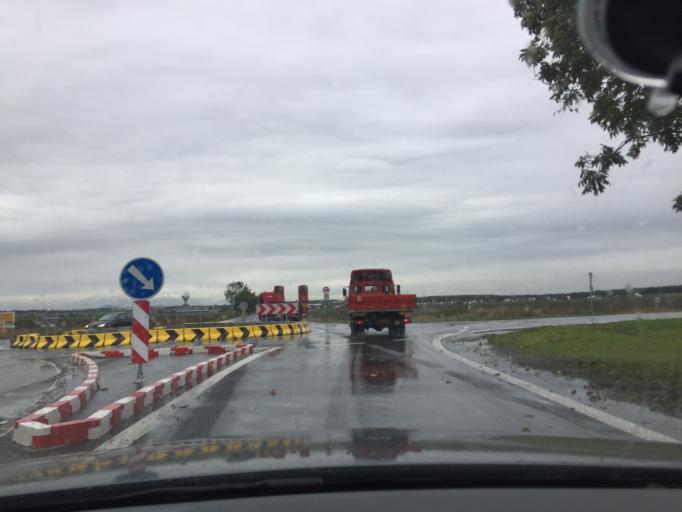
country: CZ
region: Central Bohemia
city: Zdiby
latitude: 50.1828
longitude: 14.4403
